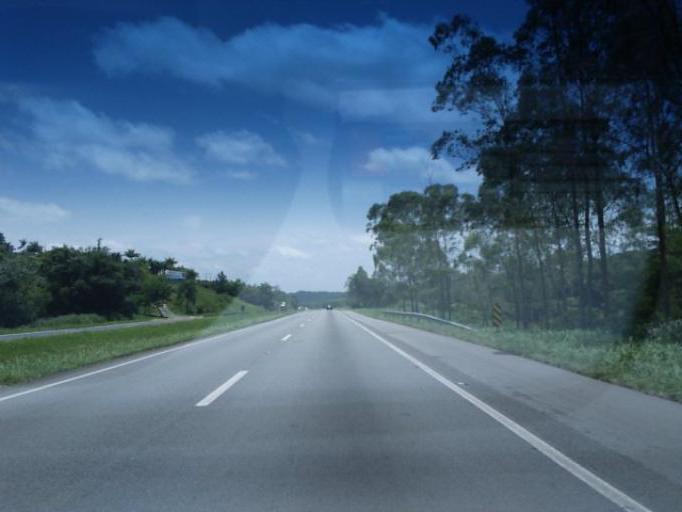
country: BR
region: Sao Paulo
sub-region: Registro
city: Registro
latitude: -24.4193
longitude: -47.7678
